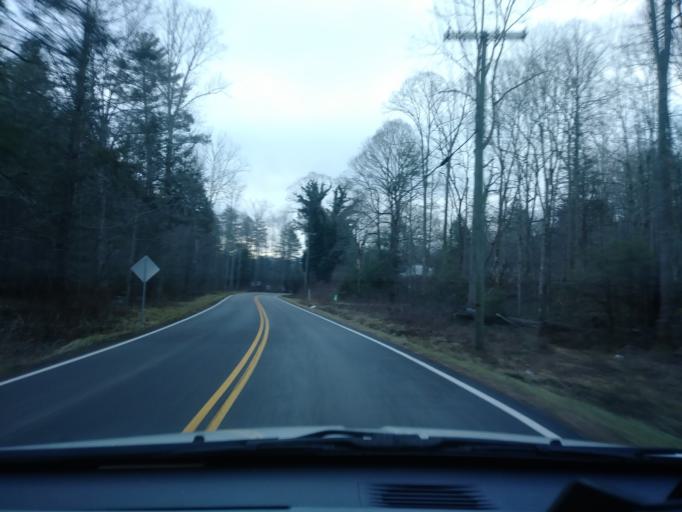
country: US
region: Tennessee
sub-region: Unicoi County
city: Unicoi
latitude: 36.1767
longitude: -82.2772
